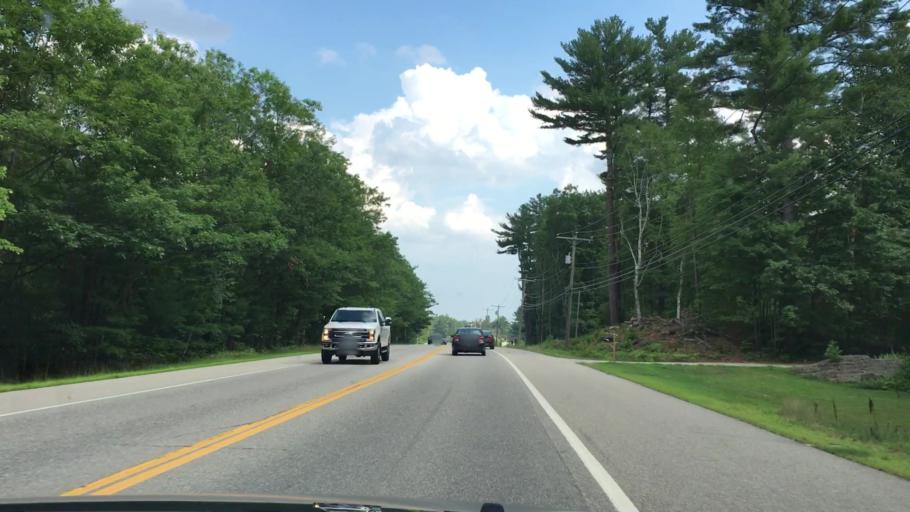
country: US
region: New Hampshire
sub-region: Strafford County
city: Farmington
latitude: 43.3466
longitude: -71.0234
